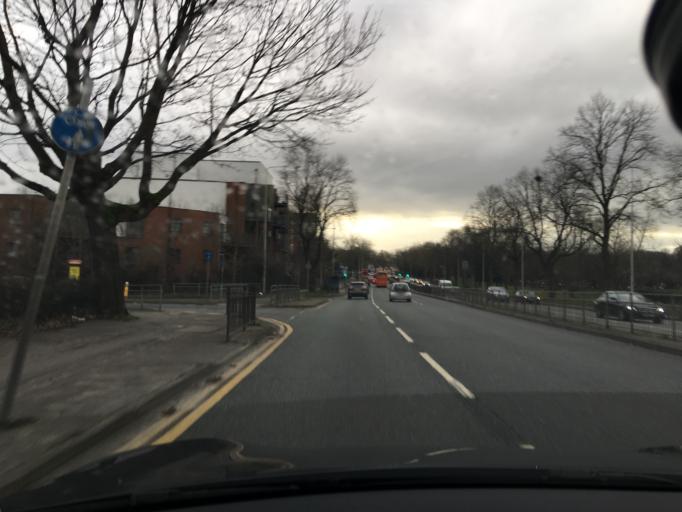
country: GB
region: England
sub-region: Manchester
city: Chorlton cum Hardy
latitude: 53.4320
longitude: -2.2492
